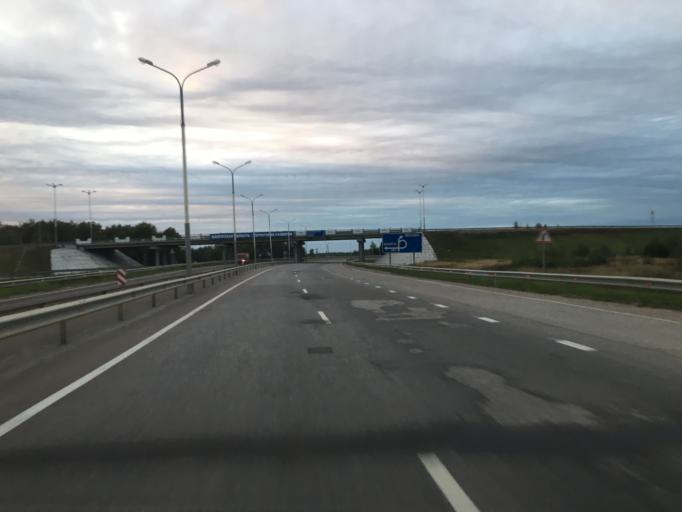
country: RU
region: Kaluga
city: Kaluga
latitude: 54.6235
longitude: 36.2905
